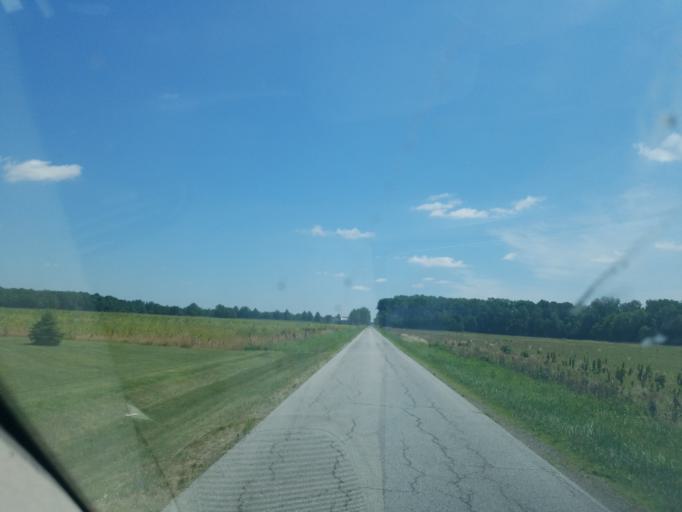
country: US
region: Ohio
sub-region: Hancock County
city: Arlington
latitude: 40.8484
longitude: -83.6329
